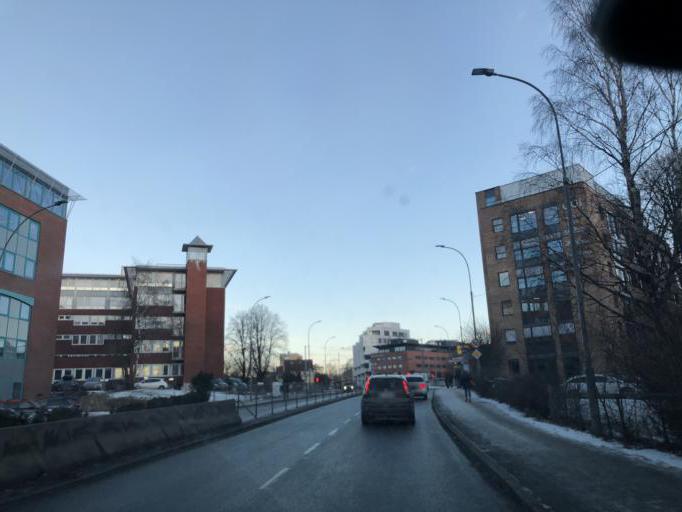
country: NO
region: Oslo
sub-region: Oslo
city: Oslo
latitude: 59.9143
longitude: 10.8006
